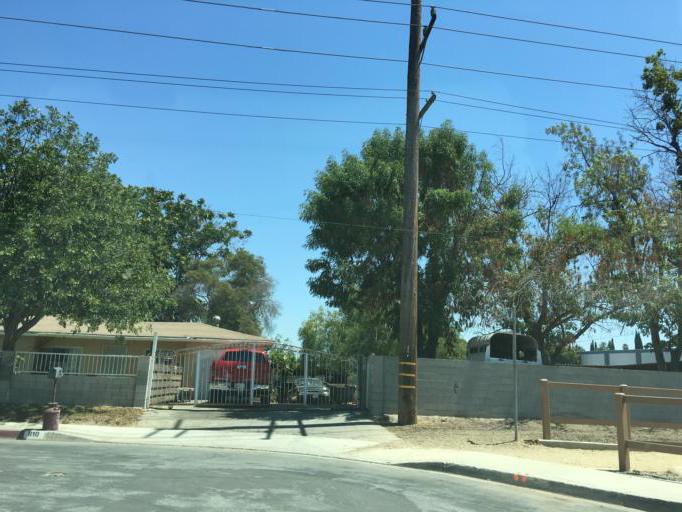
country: US
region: California
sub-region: Los Angeles County
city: Avocado Heights
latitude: 34.0292
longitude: -117.9924
